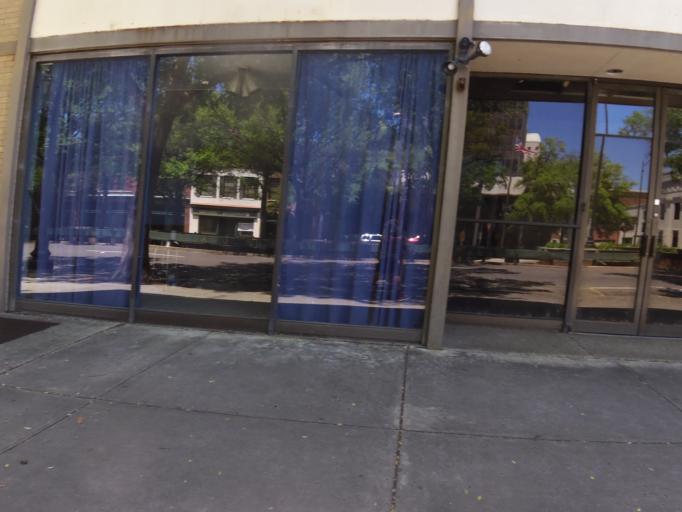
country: US
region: Georgia
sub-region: Richmond County
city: Augusta
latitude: 33.4743
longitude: -81.9631
